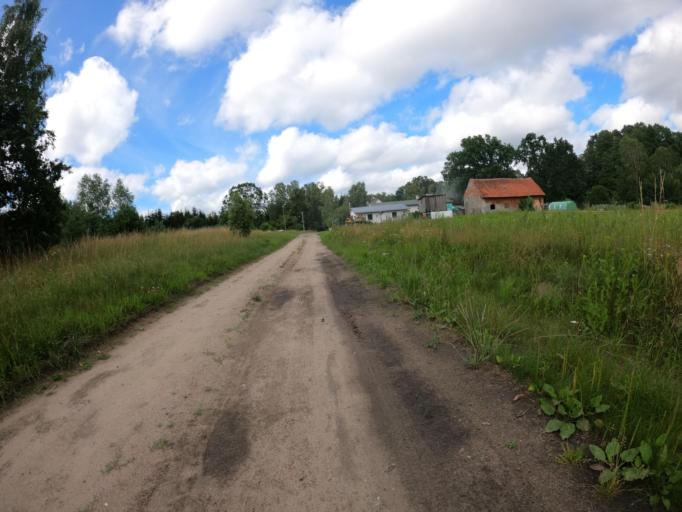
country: PL
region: West Pomeranian Voivodeship
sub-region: Powiat bialogardzki
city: Tychowo
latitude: 54.0194
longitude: 16.3538
